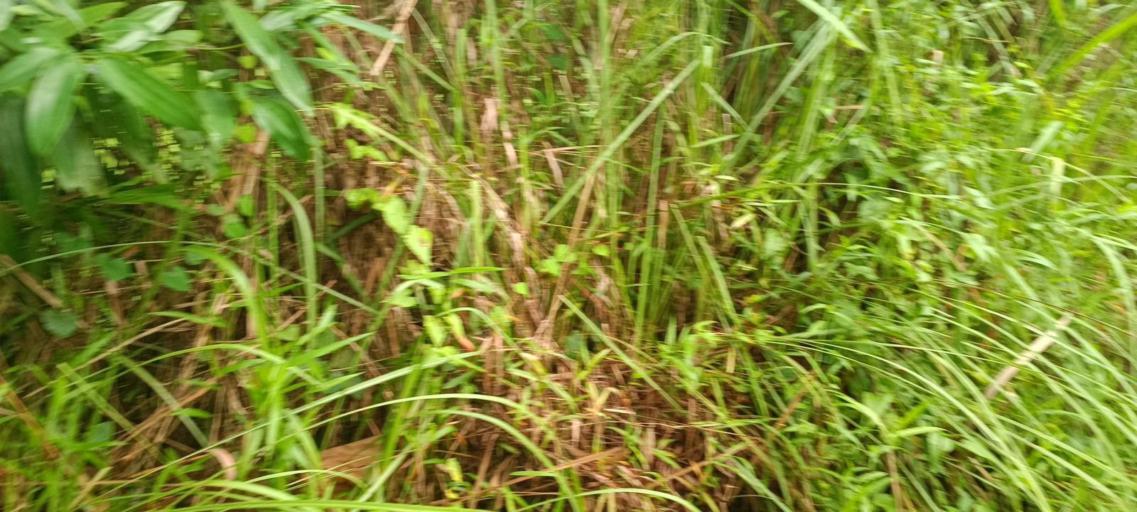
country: MY
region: Penang
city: Bukit Mertajam
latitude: 5.3754
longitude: 100.4750
